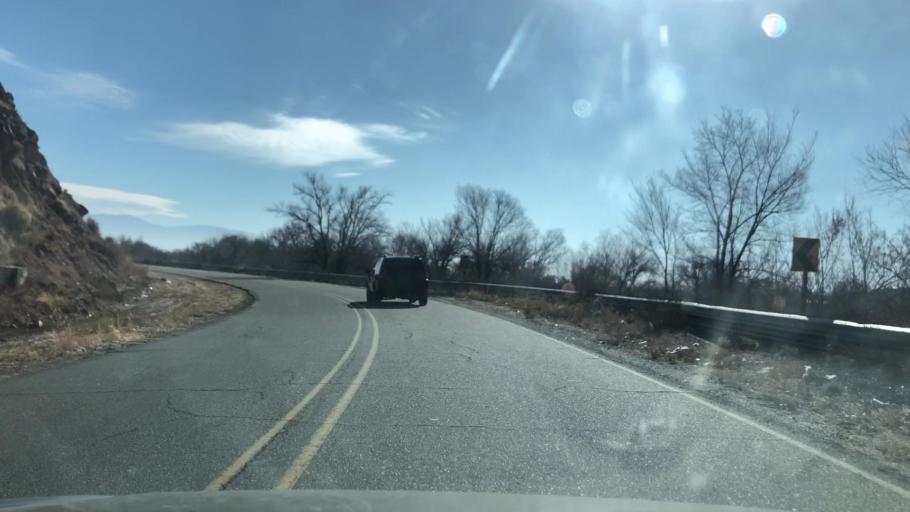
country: US
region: New Mexico
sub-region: Rio Arriba County
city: Ohkay Owingeh
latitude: 36.0852
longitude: -106.1268
